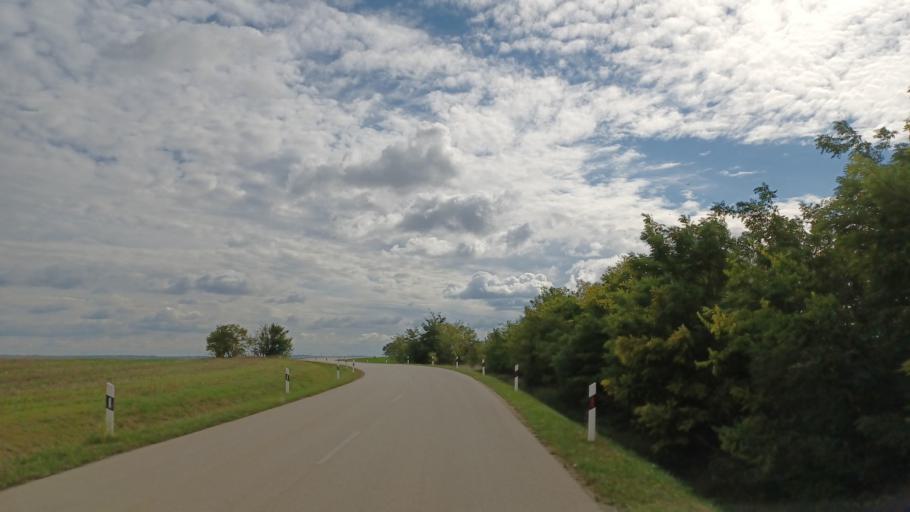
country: HU
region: Tolna
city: Simontornya
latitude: 46.7266
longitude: 18.5728
